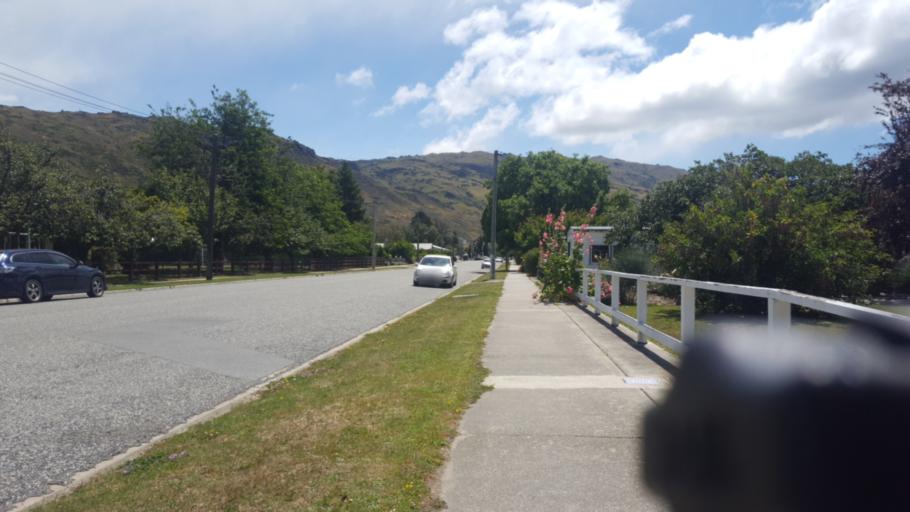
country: NZ
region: Otago
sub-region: Queenstown-Lakes District
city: Wanaka
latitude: -45.1910
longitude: 169.3198
